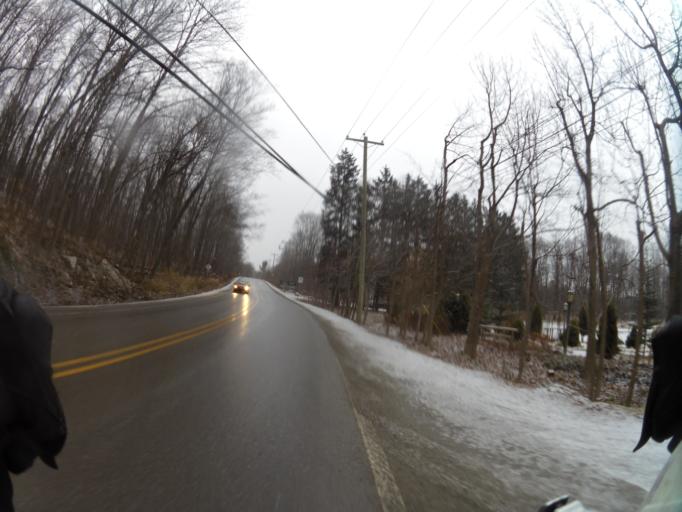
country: CA
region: Quebec
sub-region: Outaouais
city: Gatineau
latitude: 45.5011
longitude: -75.8132
